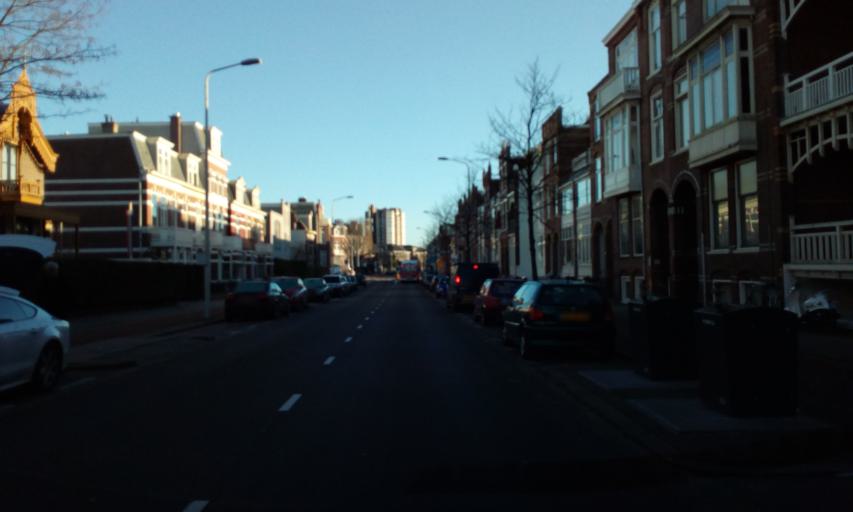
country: NL
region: South Holland
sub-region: Gemeente Den Haag
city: Scheveningen
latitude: 52.1119
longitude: 4.2858
